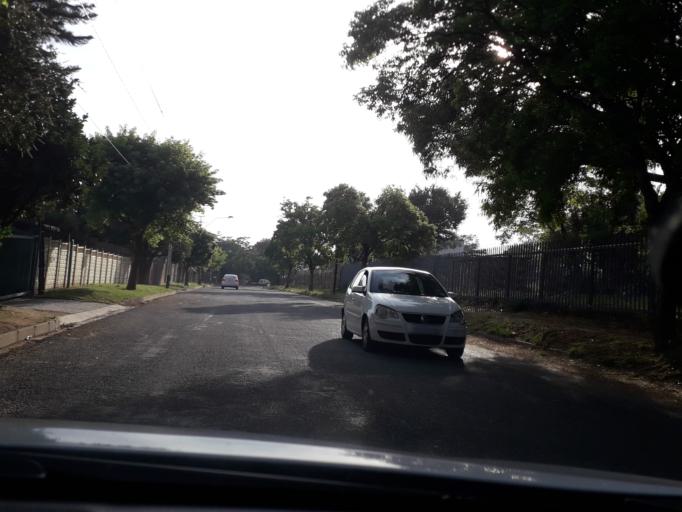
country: ZA
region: Gauteng
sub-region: City of Johannesburg Metropolitan Municipality
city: Johannesburg
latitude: -26.1333
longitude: 28.0902
